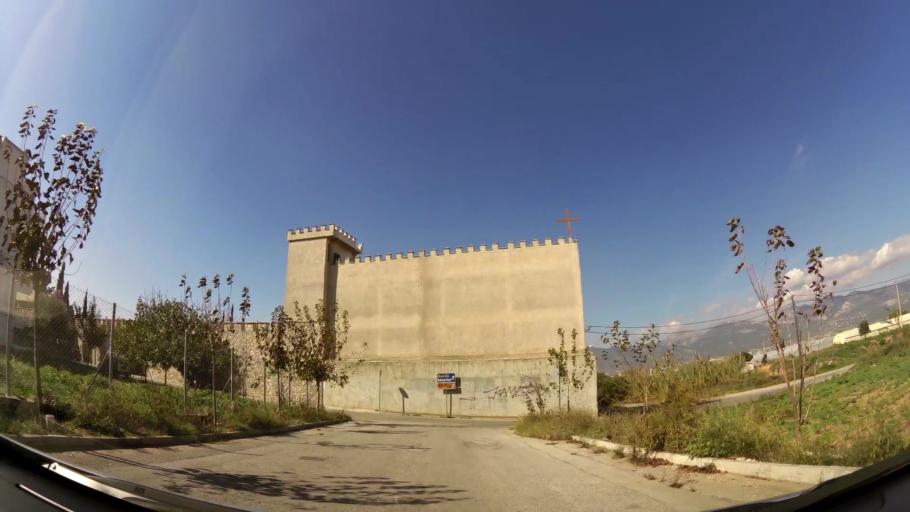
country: GR
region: Attica
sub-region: Nomarchia Athinas
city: Lykovrysi
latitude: 38.0757
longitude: 23.7861
